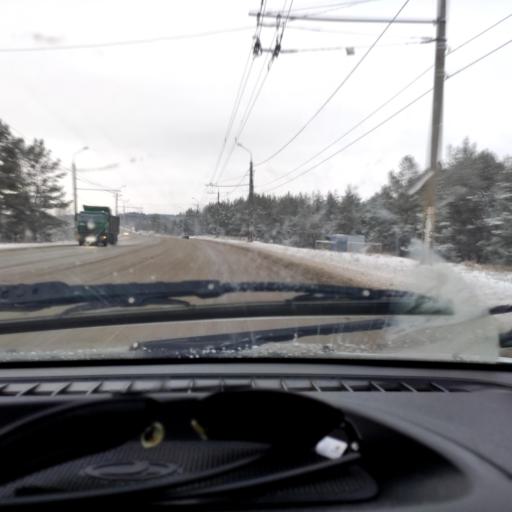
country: RU
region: Samara
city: Zhigulevsk
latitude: 53.4994
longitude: 49.5120
